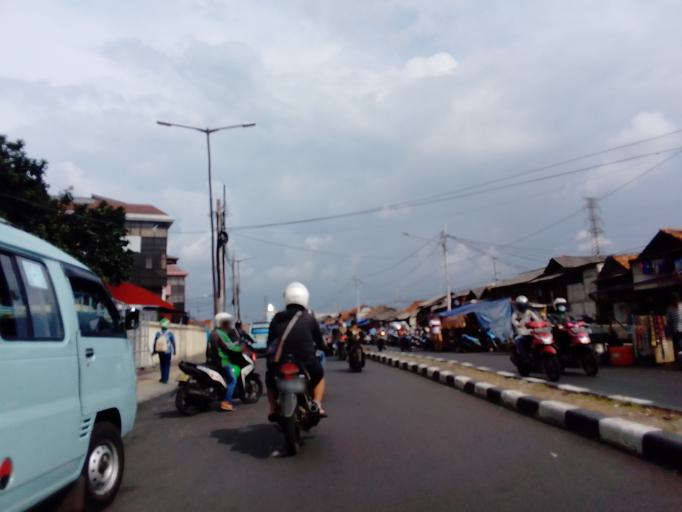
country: ID
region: Jakarta Raya
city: Jakarta
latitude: -6.1673
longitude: 106.8023
